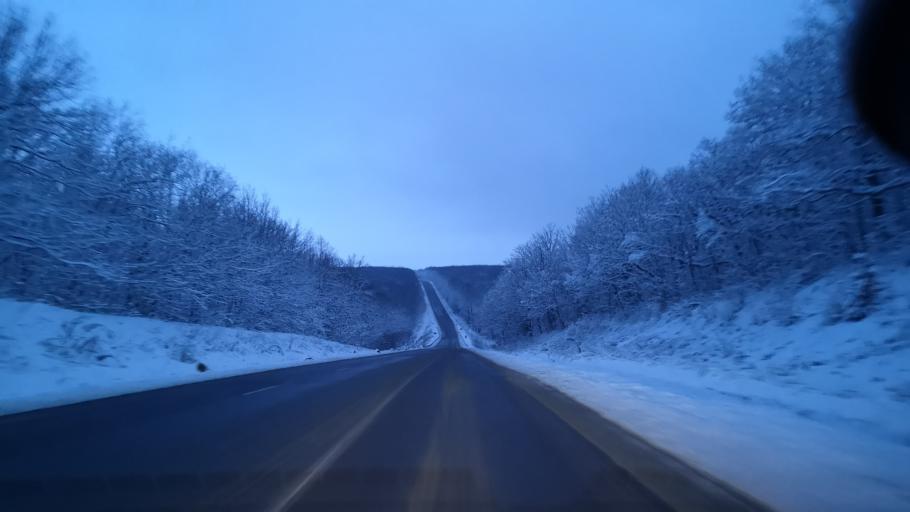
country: MD
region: Rezina
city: Rezina
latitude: 47.7291
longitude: 28.8672
